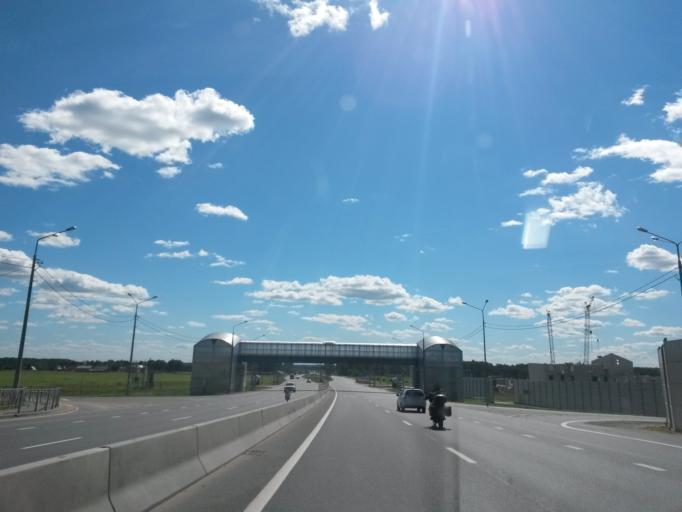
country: RU
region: Jaroslavl
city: Yaroslavl
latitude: 57.7036
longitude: 39.8999
